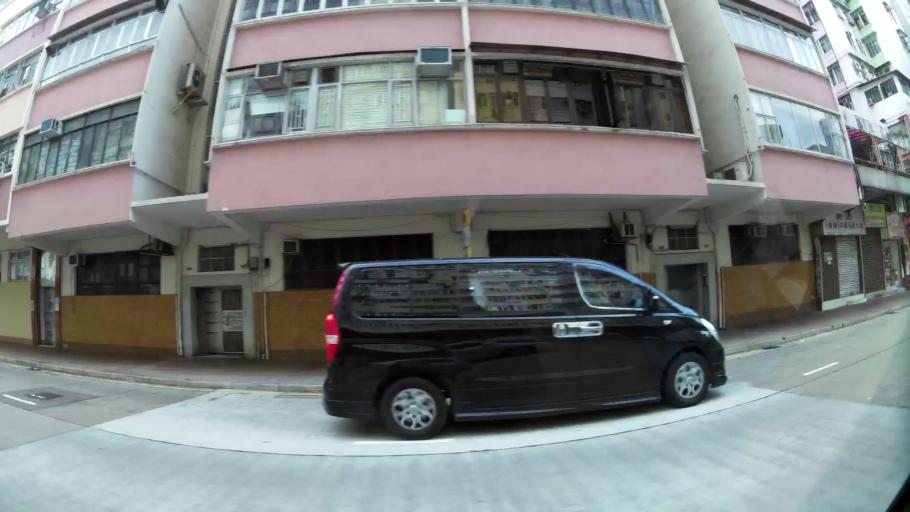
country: HK
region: Sham Shui Po
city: Sham Shui Po
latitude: 22.3244
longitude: 114.1648
